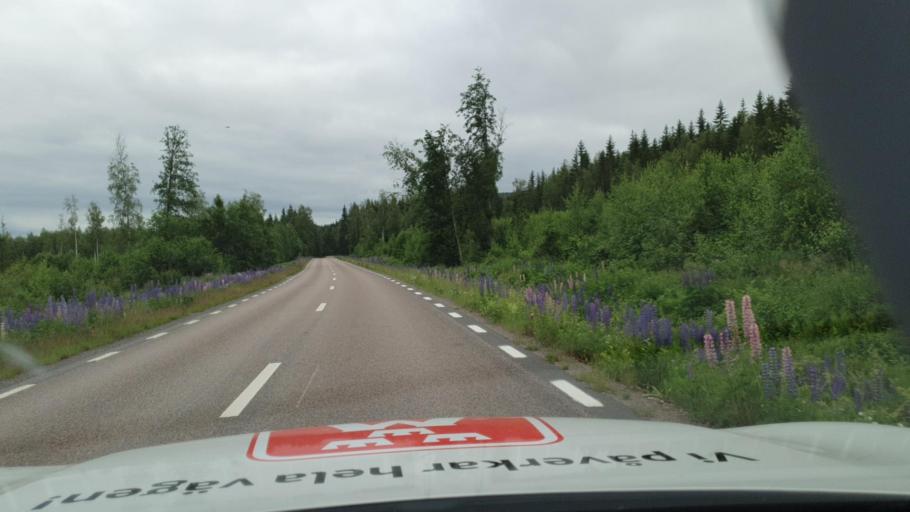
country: SE
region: Vaermland
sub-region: Sunne Kommun
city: Sunne
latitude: 59.8324
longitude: 12.9701
